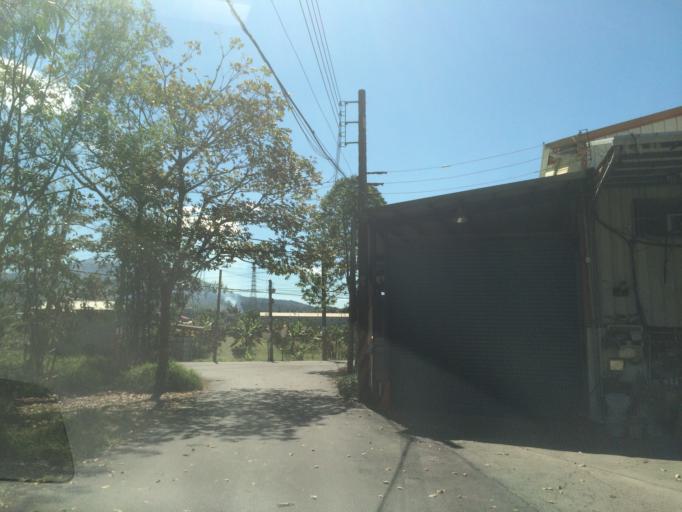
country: TW
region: Taiwan
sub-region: Yunlin
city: Douliu
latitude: 23.7017
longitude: 120.6109
